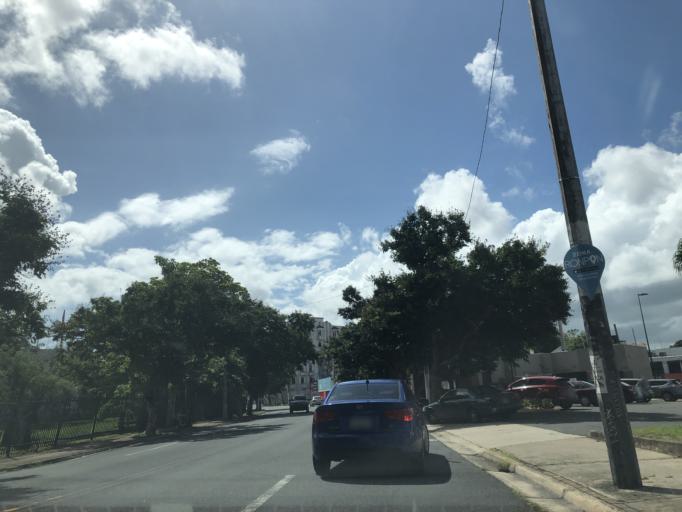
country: PR
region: Trujillo Alto
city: Trujillo Alto
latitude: 18.4023
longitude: -66.0531
